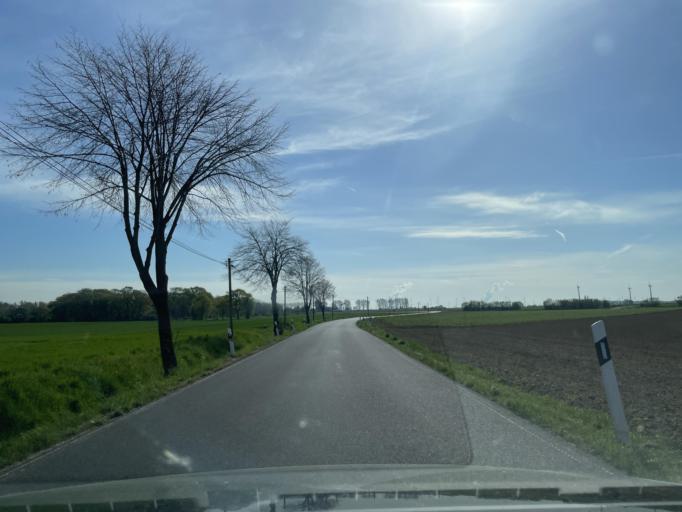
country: DE
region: North Rhine-Westphalia
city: Erkelenz
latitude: 51.0795
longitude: 6.3850
